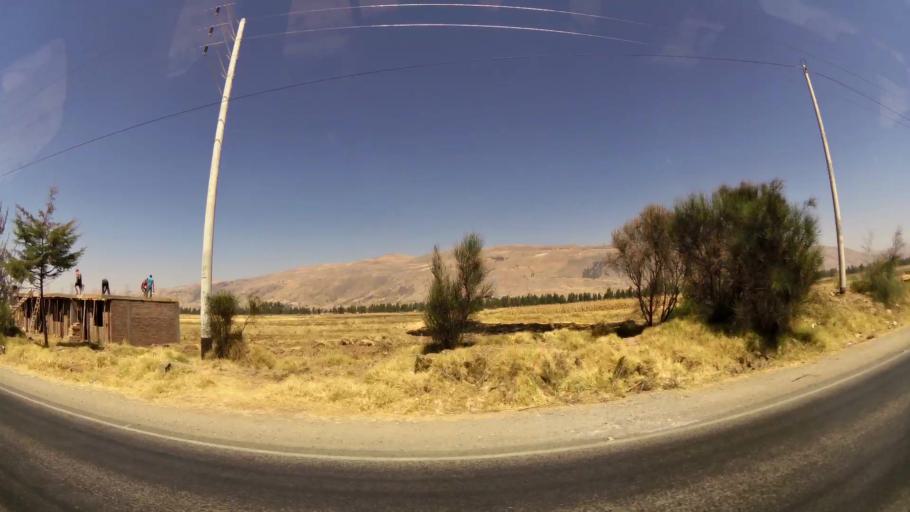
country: PE
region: Junin
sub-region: Provincia de Jauja
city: Huamali
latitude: -11.8228
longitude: -75.4120
